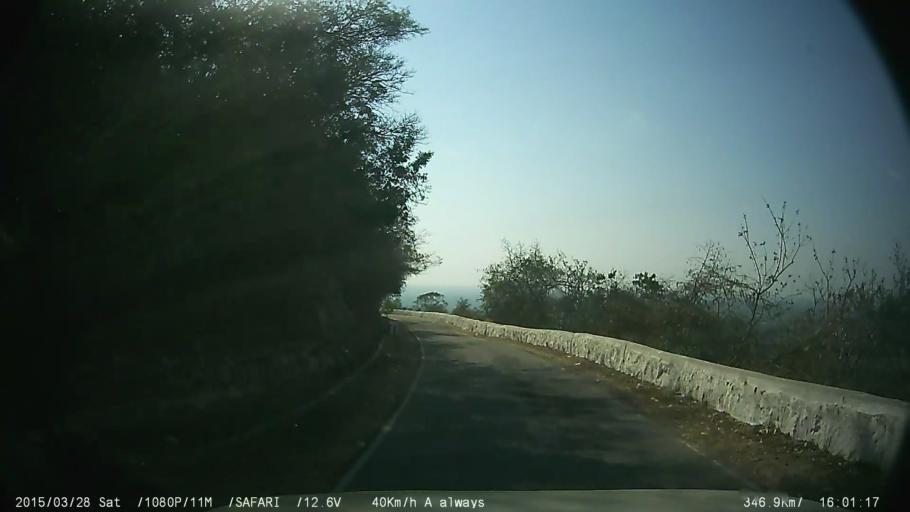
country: IN
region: Karnataka
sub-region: Mysore
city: Mysore
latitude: 12.2804
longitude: 76.6722
